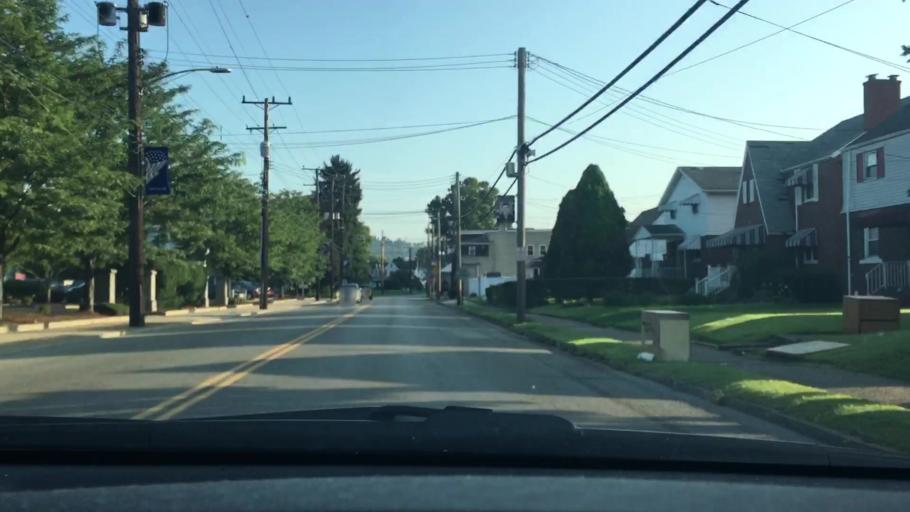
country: US
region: Pennsylvania
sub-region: Allegheny County
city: Glassport
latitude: 40.3356
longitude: -79.8906
